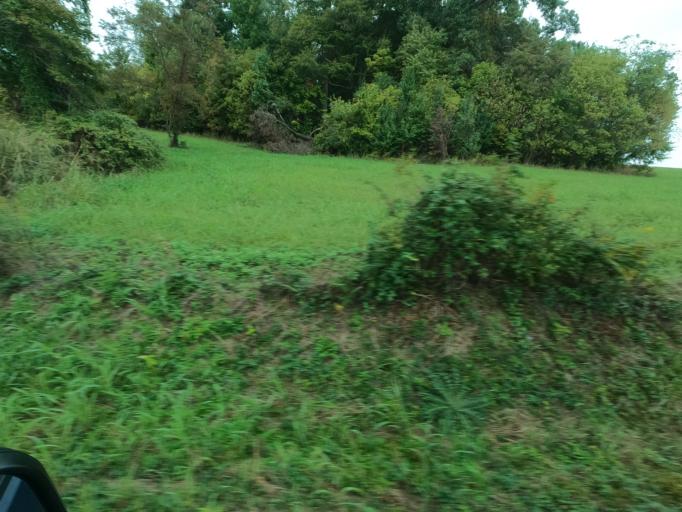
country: US
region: Tennessee
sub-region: Washington County
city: Oak Grove
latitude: 36.3888
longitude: -82.4167
